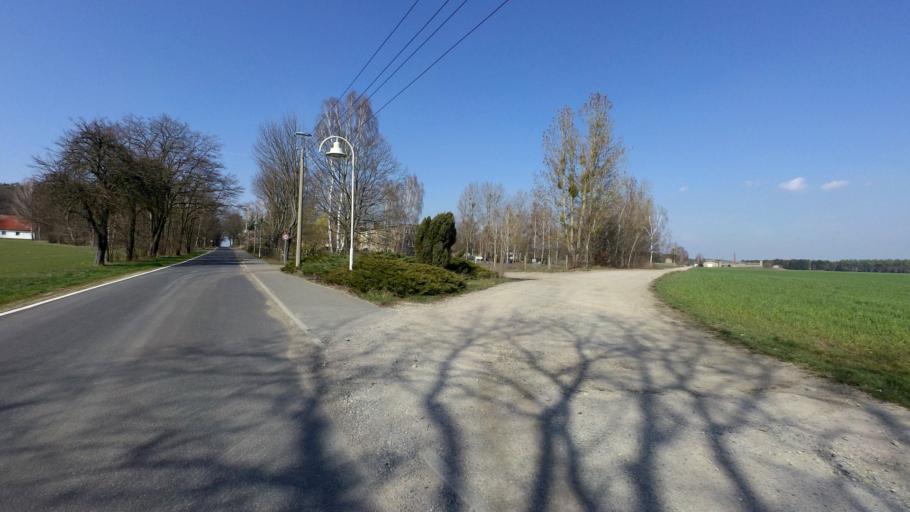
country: DE
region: Brandenburg
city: Drahnsdorf
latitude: 51.9188
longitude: 13.5767
